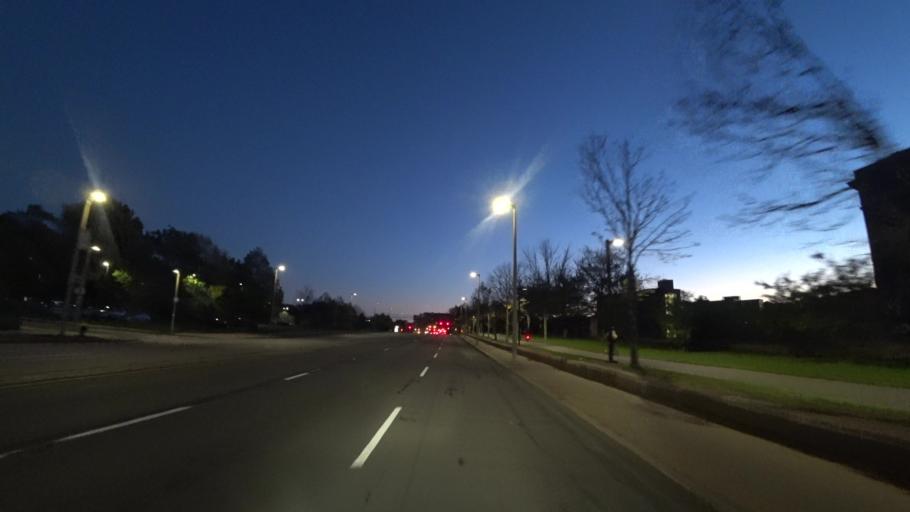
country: US
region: Massachusetts
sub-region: Norfolk County
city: Brookline
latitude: 42.3267
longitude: -71.0979
